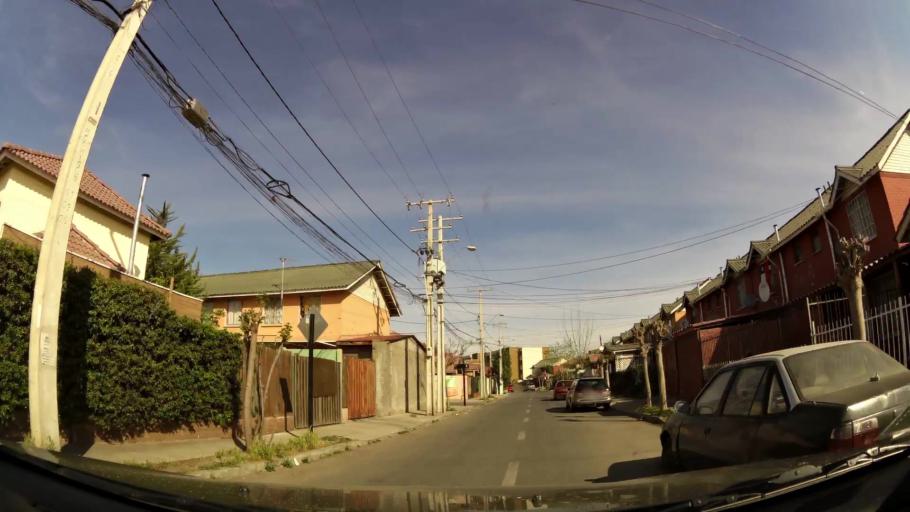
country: CL
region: Santiago Metropolitan
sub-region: Provincia de Cordillera
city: Puente Alto
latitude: -33.5879
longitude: -70.5517
